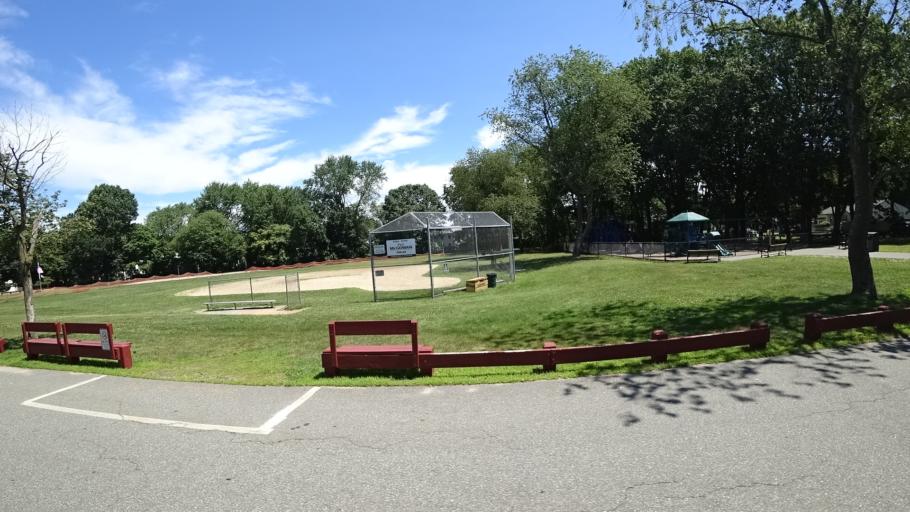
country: US
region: Massachusetts
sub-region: Norfolk County
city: Dedham
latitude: 42.2330
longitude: -71.1538
